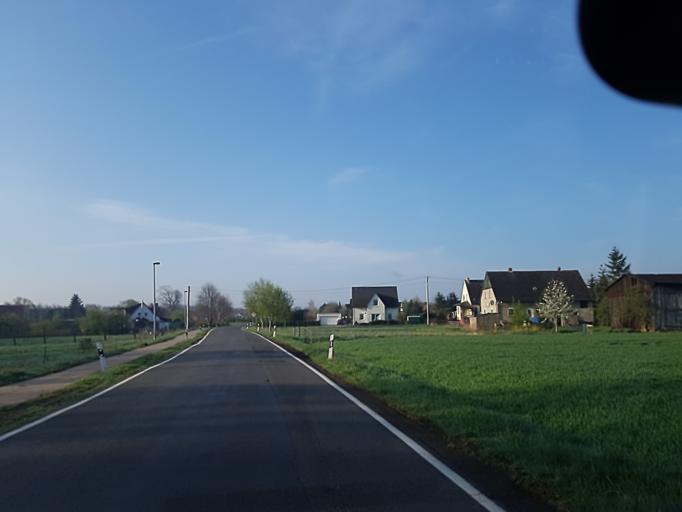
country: DE
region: Saxony
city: Oschatz
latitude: 51.3443
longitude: 13.0917
